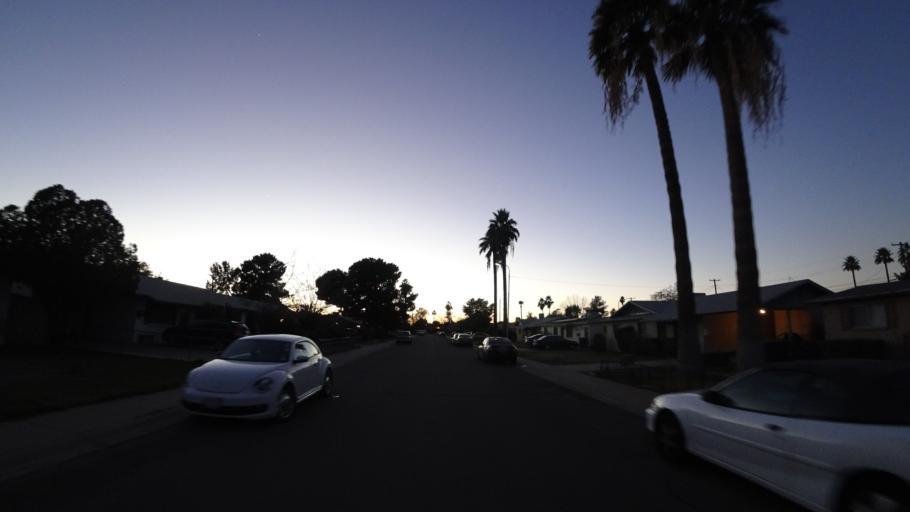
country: US
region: Arizona
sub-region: Maricopa County
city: Tempe Junction
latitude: 33.4123
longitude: -111.9587
